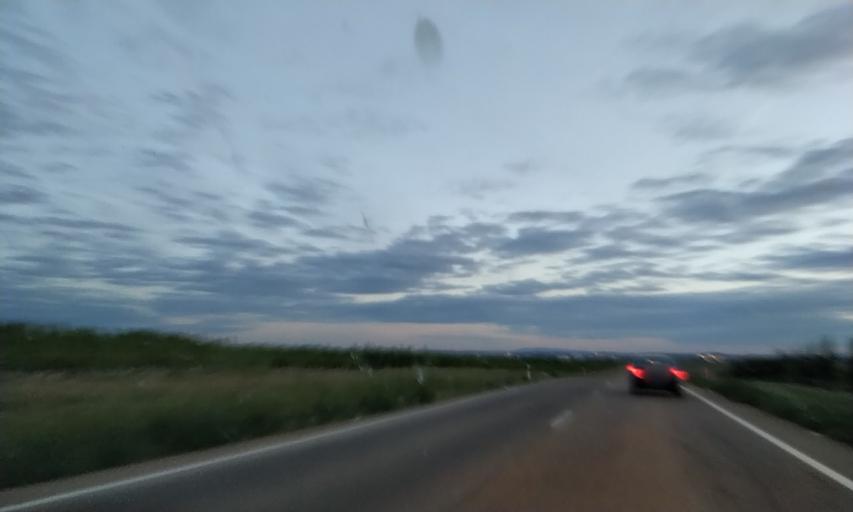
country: ES
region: Extremadura
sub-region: Provincia de Badajoz
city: Badajoz
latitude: 38.9420
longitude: -6.9193
